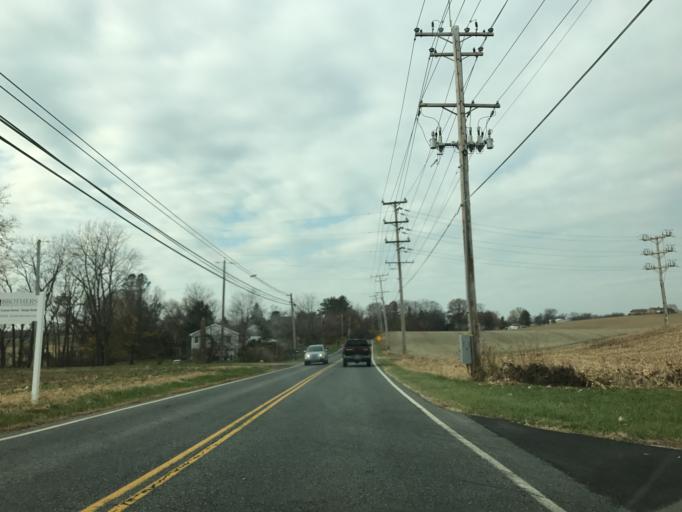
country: US
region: Maryland
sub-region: Harford County
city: Bel Air North
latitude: 39.5803
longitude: -76.4103
